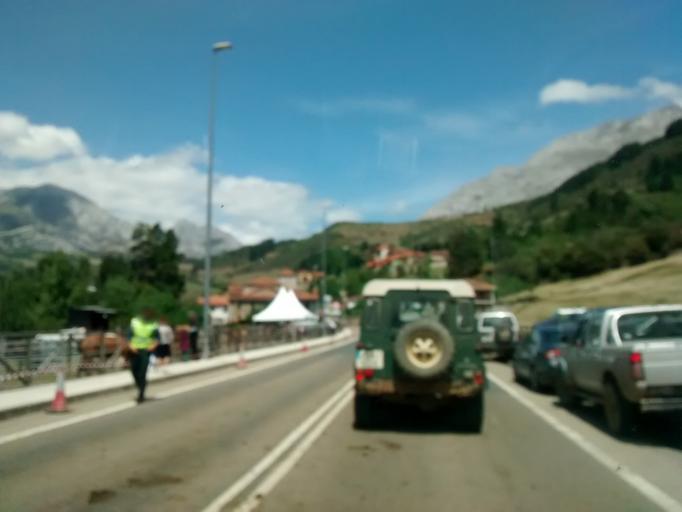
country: ES
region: Cantabria
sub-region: Provincia de Cantabria
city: Potes
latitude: 43.1737
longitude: -4.6009
